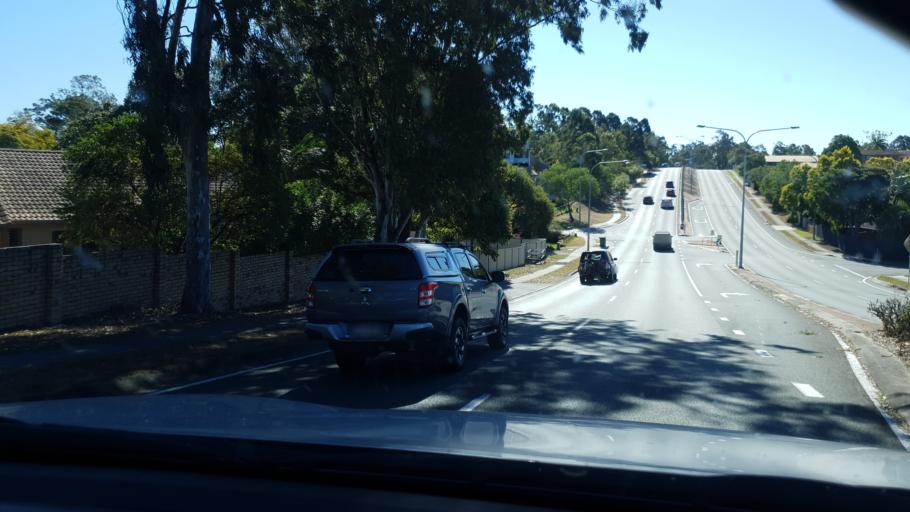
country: AU
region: Queensland
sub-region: Brisbane
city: Everton Park
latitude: -27.3966
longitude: 152.9867
